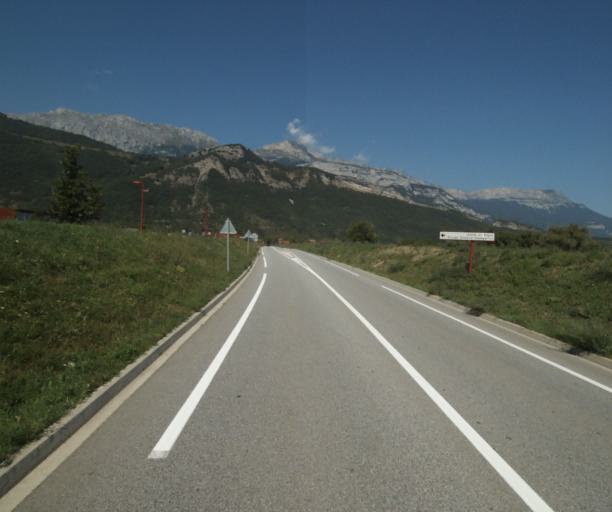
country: FR
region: Rhone-Alpes
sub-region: Departement de l'Isere
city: Vif
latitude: 45.0588
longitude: 5.6817
